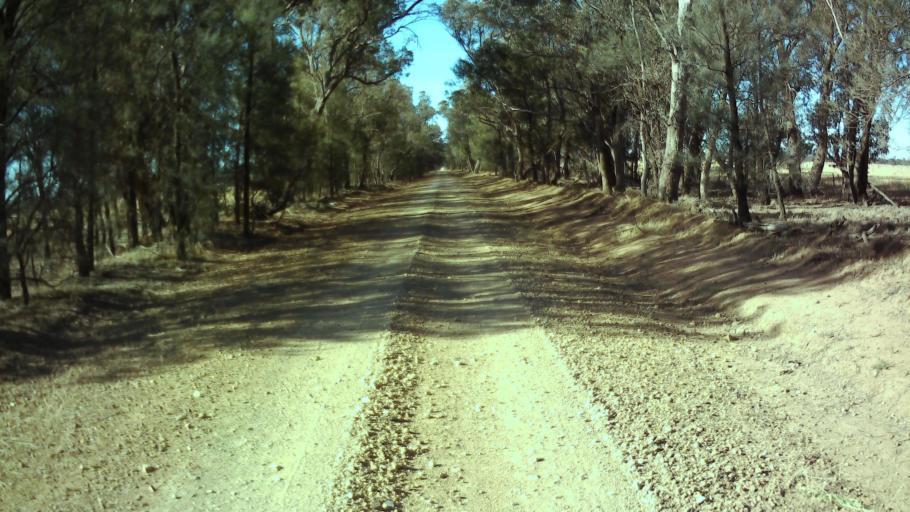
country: AU
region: New South Wales
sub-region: Weddin
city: Grenfell
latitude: -33.8214
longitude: 147.8753
